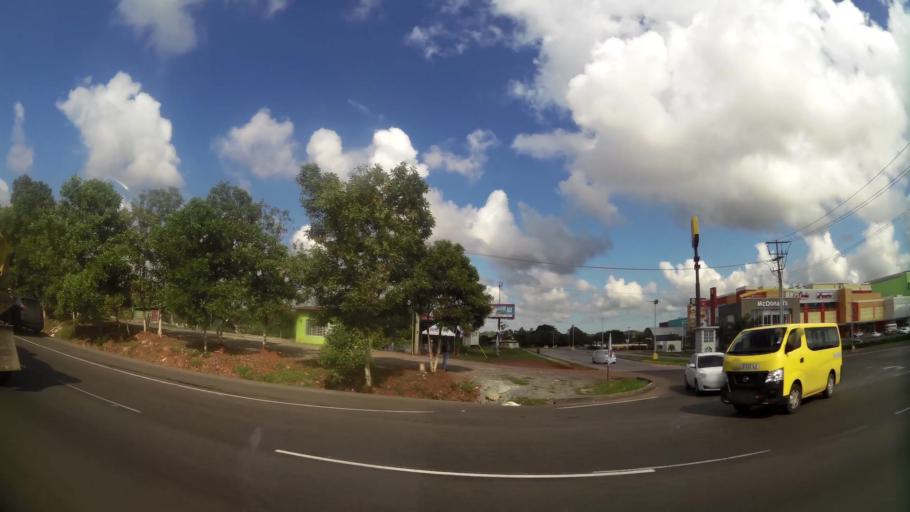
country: PA
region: Panama
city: Nuevo Arraijan
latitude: 8.9186
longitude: -79.7064
